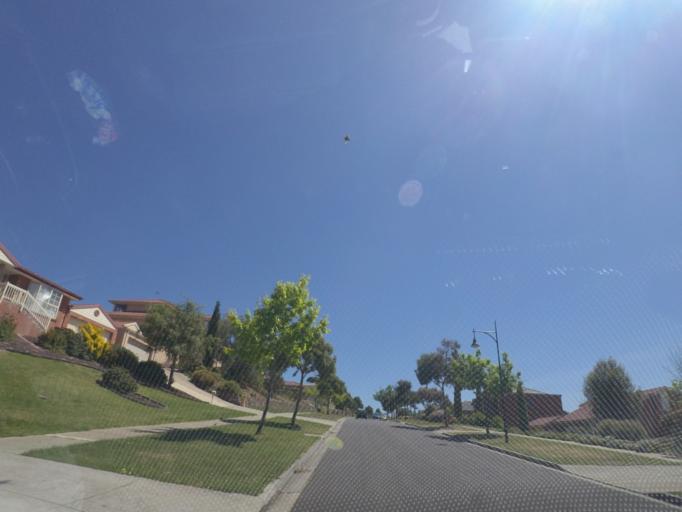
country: AU
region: Victoria
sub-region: Hume
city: Sunbury
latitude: -37.5568
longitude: 144.7117
